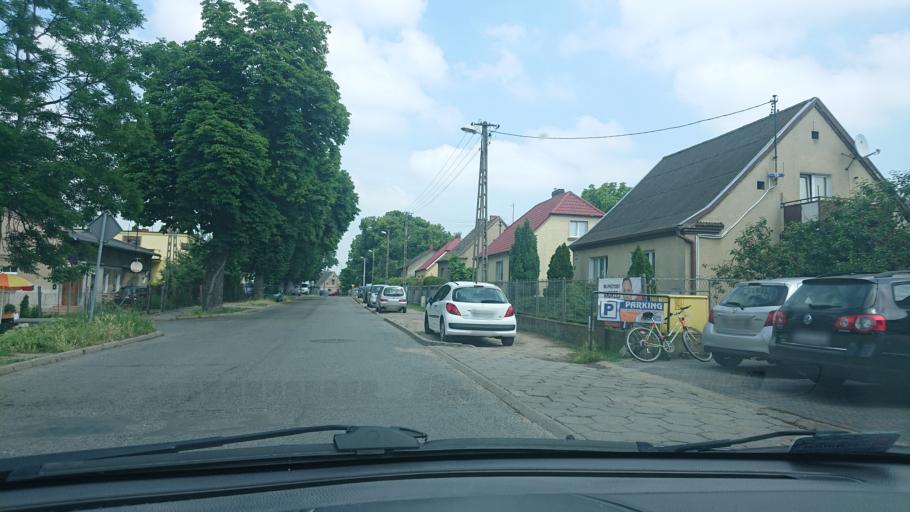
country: PL
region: Greater Poland Voivodeship
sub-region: Powiat gnieznienski
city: Gniezno
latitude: 52.5211
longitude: 17.5806
